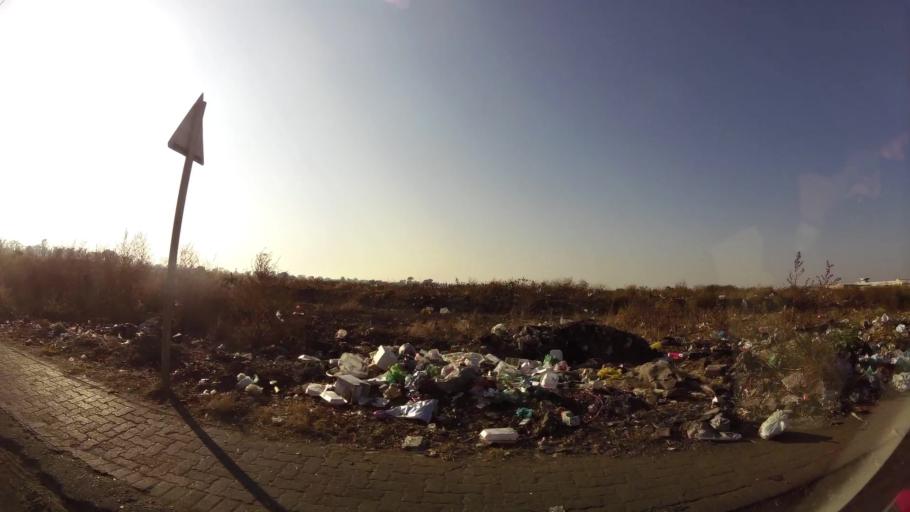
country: ZA
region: Orange Free State
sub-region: Mangaung Metropolitan Municipality
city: Bloemfontein
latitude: -29.1376
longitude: 26.2518
